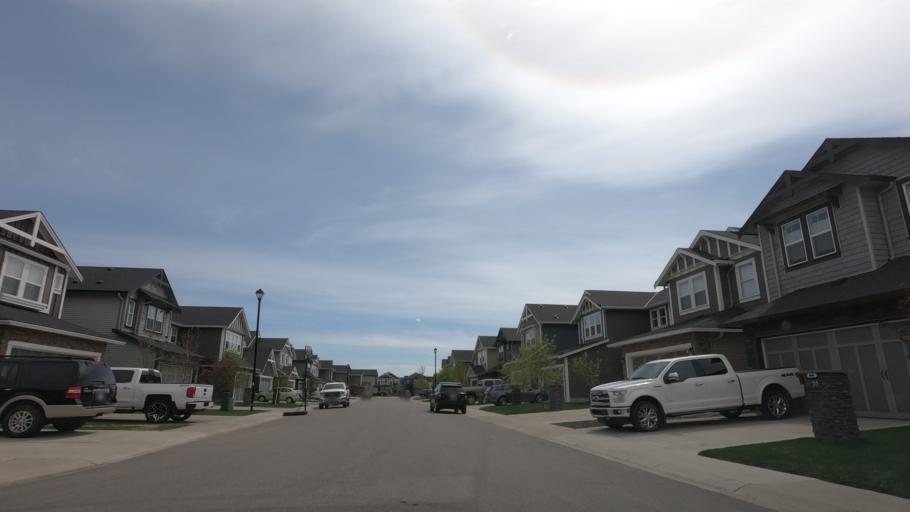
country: CA
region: Alberta
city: Airdrie
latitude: 51.3061
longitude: -114.0348
